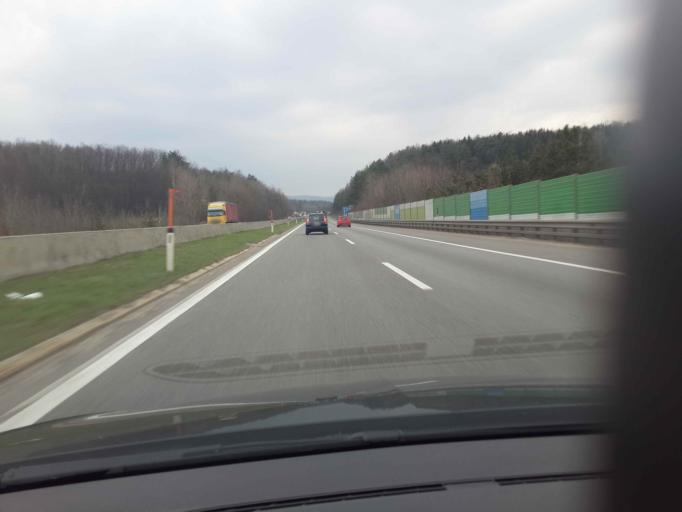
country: AT
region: Lower Austria
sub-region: Politischer Bezirk Modling
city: Gaaden
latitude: 48.0682
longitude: 16.1683
